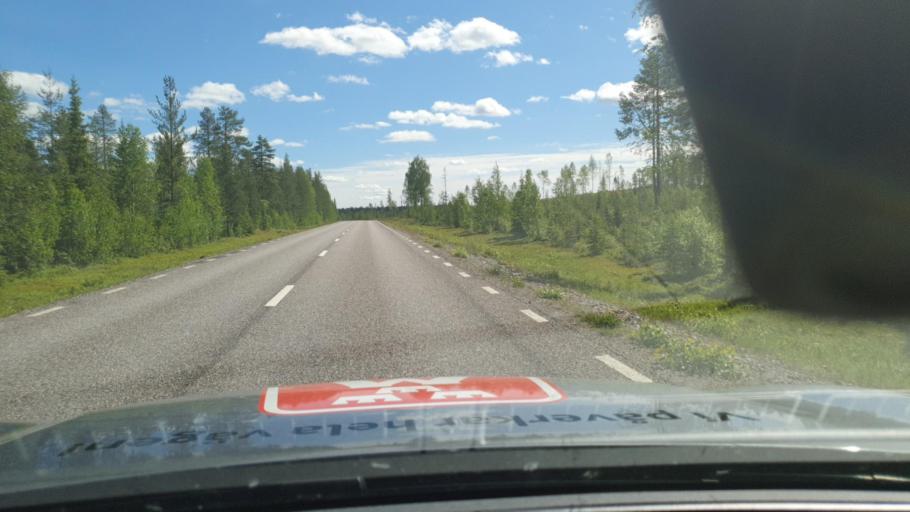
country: SE
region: Norrbotten
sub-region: Pajala Kommun
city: Pajala
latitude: 67.1712
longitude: 23.5140
